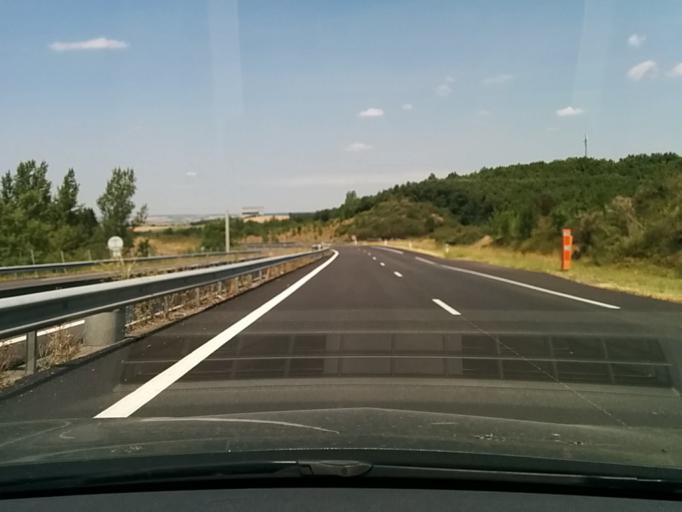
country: FR
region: Midi-Pyrenees
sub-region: Departement du Gers
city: Pujaudran
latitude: 43.5901
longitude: 1.1268
